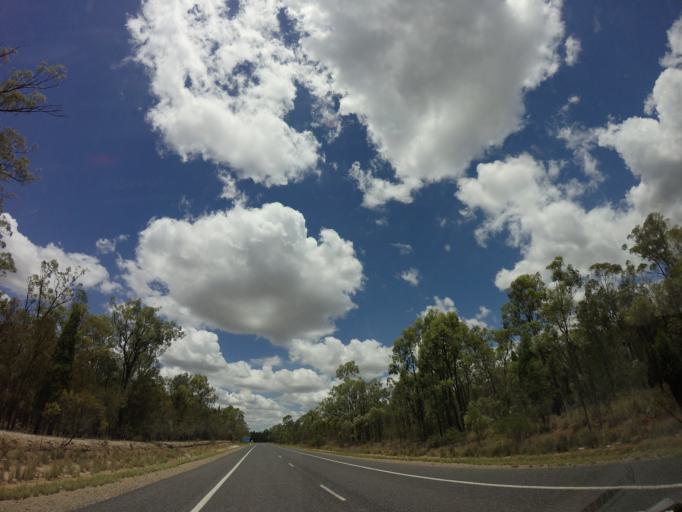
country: AU
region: Queensland
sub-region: Western Downs
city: Dalby
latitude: -27.9770
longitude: 151.0854
